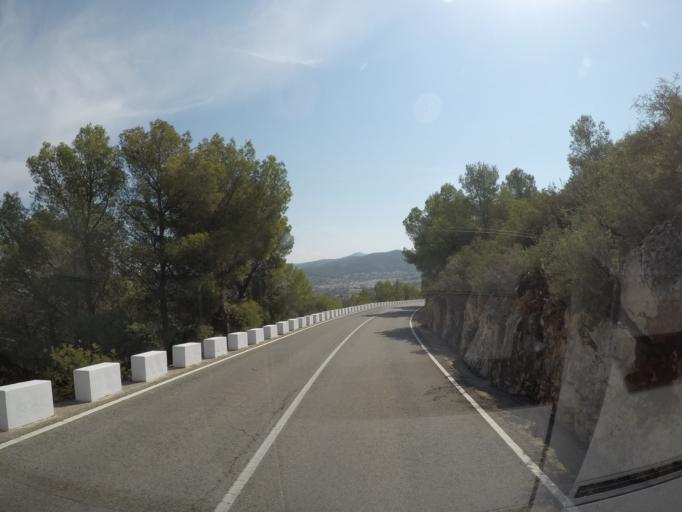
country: ES
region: Valencia
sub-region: Provincia de Alicante
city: Tormos
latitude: 38.7856
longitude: -0.0835
